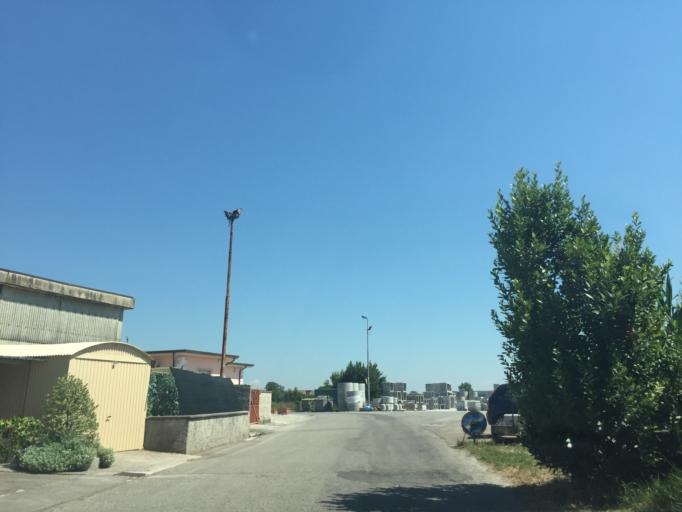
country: IT
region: Tuscany
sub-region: Provincia di Pistoia
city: Anchione
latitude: 43.8208
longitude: 10.7575
